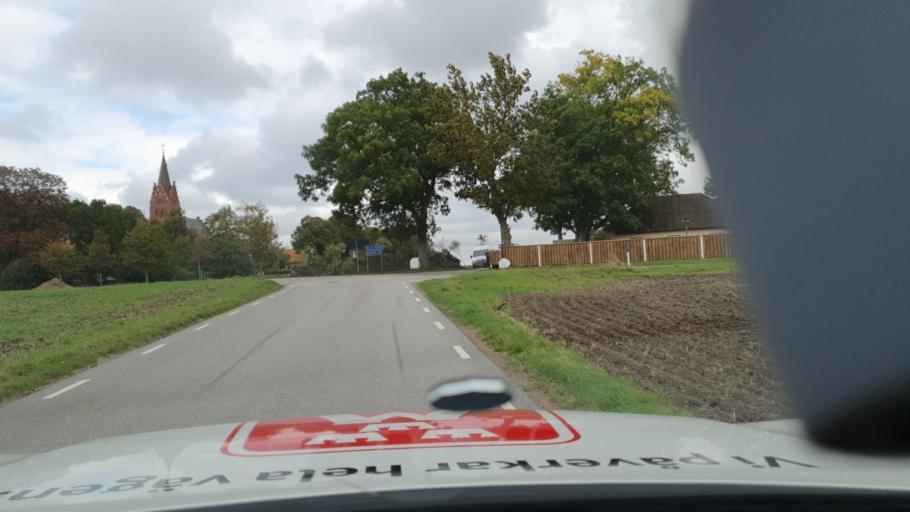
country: SE
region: Skane
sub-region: Vellinge Kommun
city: Vellinge
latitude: 55.4468
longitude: 13.0807
